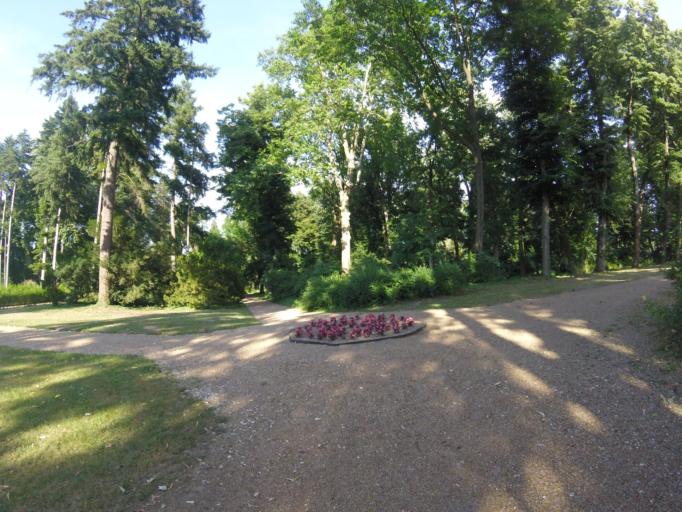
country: HU
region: Baranya
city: Sellye
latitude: 45.8696
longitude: 17.8469
